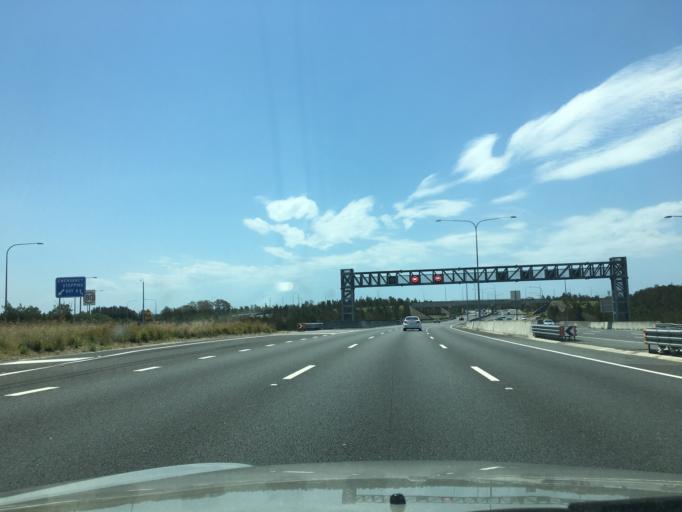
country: AU
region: Queensland
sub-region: Brisbane
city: Ascot
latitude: -27.4092
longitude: 153.0881
